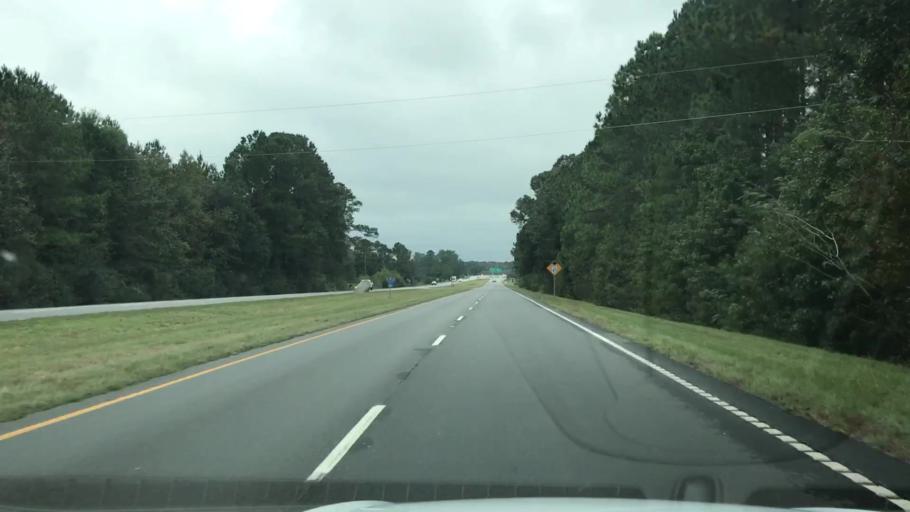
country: US
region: South Carolina
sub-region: Hampton County
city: Yemassee
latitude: 32.5942
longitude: -80.7523
